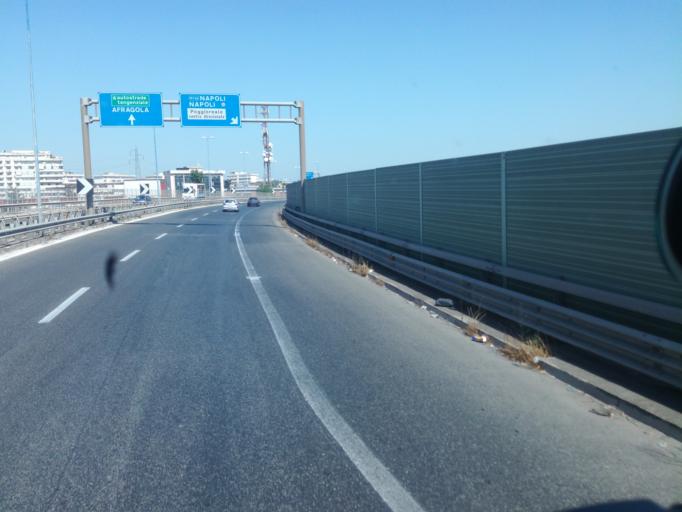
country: IT
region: Campania
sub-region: Provincia di Napoli
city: Arpino
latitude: 40.8917
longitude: 14.3259
